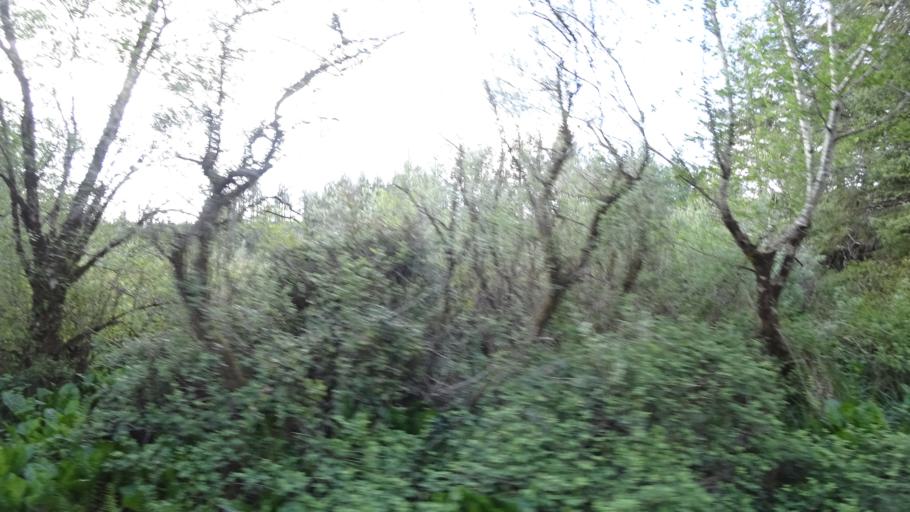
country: US
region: Oregon
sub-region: Douglas County
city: Reedsport
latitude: 43.7553
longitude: -124.1402
